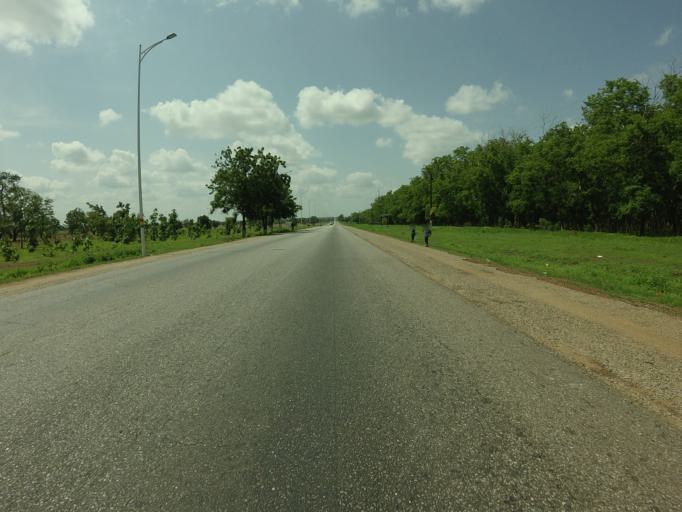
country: GH
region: Northern
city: Savelugu
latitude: 9.5398
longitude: -0.8392
